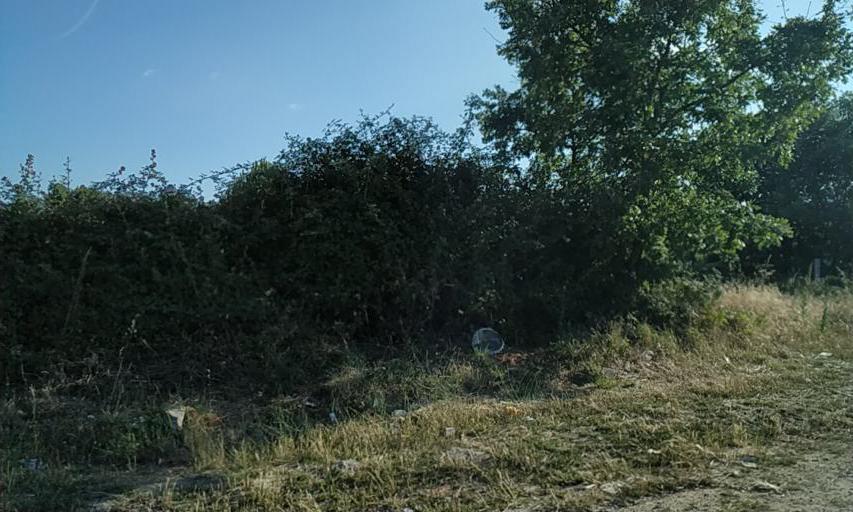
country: PT
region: Vila Real
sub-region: Chaves
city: Chaves
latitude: 41.7693
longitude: -7.4656
